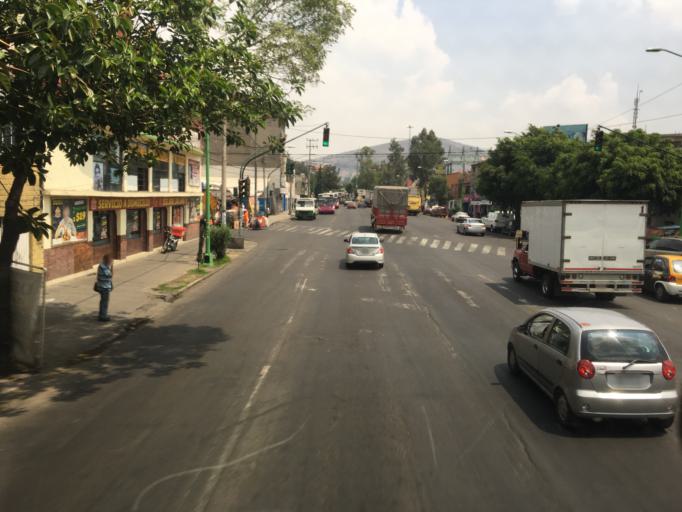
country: MX
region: Mexico
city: Colonia Lindavista
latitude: 19.5199
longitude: -99.1569
